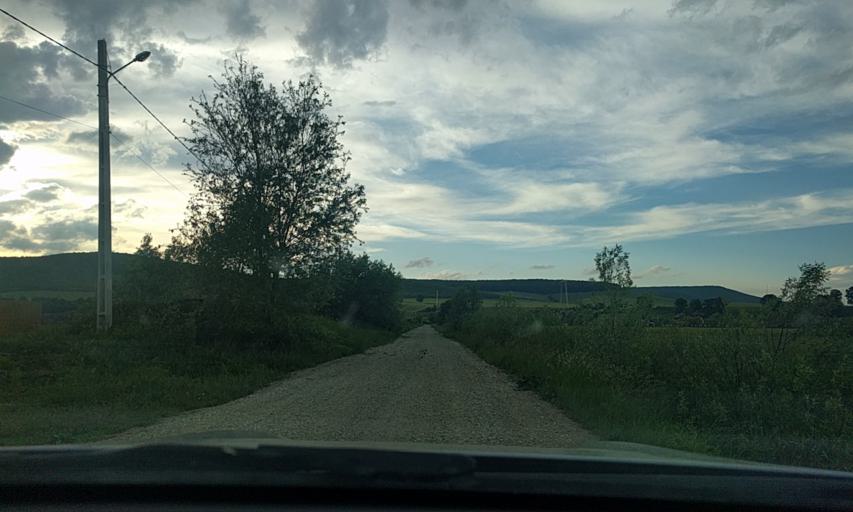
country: RO
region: Covasna
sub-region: Comuna Ilieni
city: Ilieni
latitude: 45.7639
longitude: 25.7198
